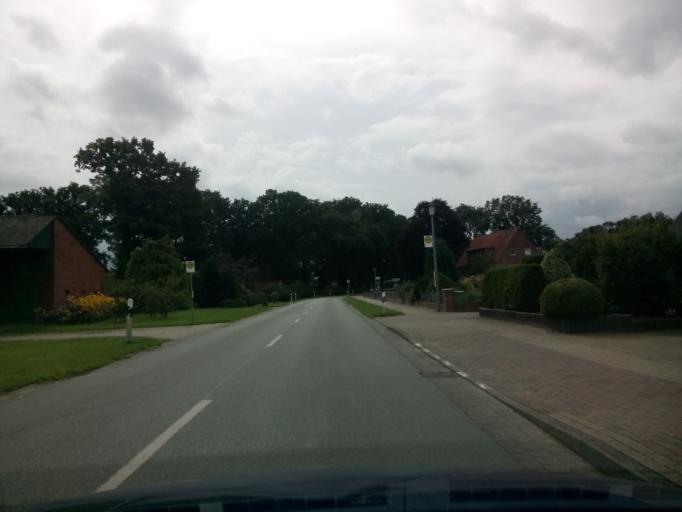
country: DE
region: Lower Saxony
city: Beverstedt
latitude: 53.4801
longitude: 8.8555
